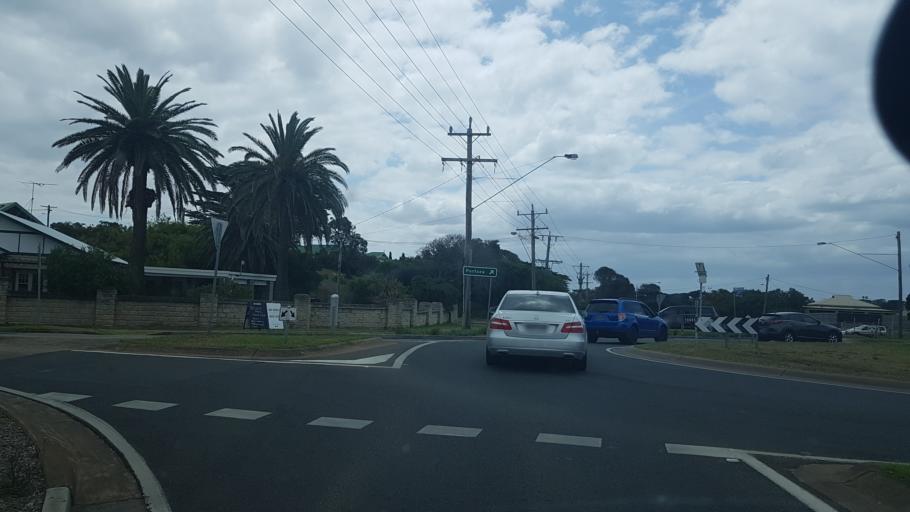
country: AU
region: Victoria
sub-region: Mornington Peninsula
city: Sorrento
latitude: -38.3403
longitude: 144.7364
